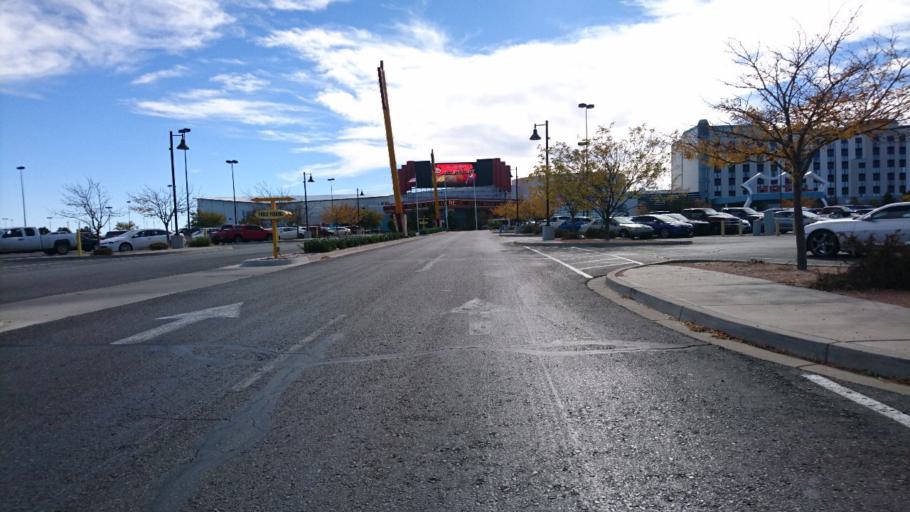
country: US
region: New Mexico
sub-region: Bernalillo County
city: South Valley
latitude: 35.0296
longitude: -106.9515
